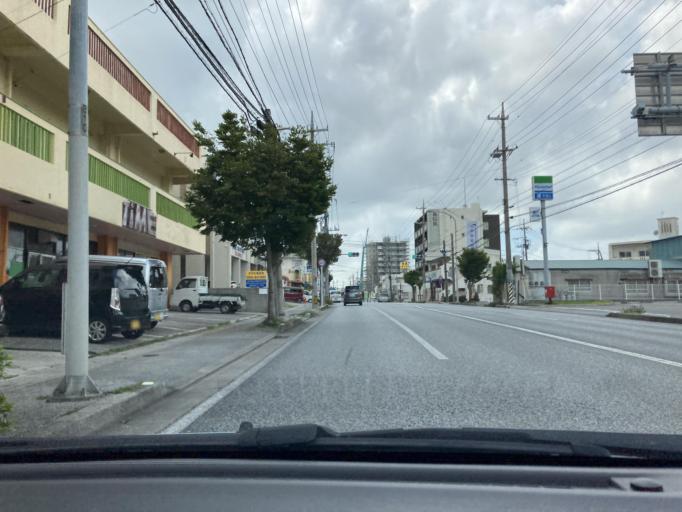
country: JP
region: Okinawa
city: Okinawa
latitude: 26.3435
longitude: 127.8200
